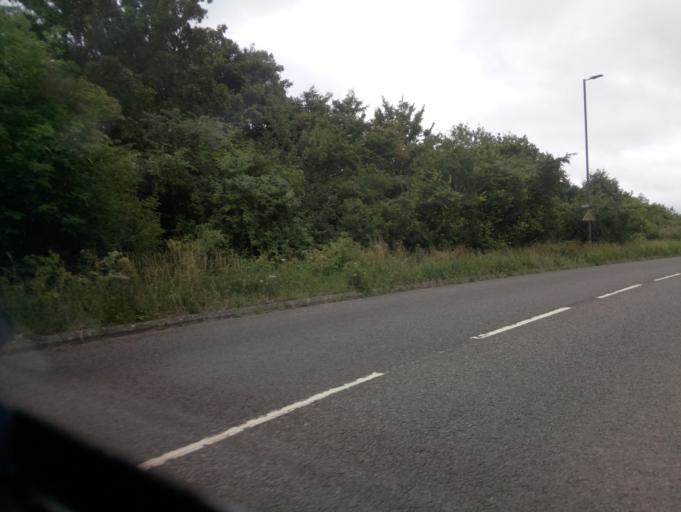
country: GB
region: England
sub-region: Gloucestershire
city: Tewkesbury
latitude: 51.9771
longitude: -2.1525
